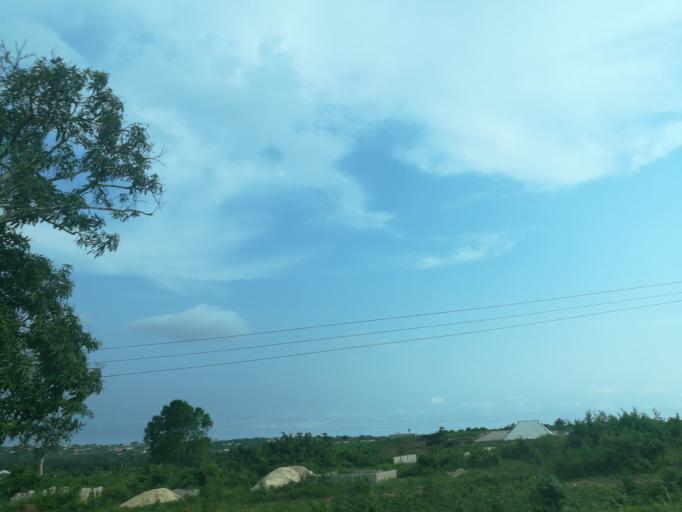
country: NG
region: Lagos
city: Ikorodu
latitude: 6.6187
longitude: 3.6530
